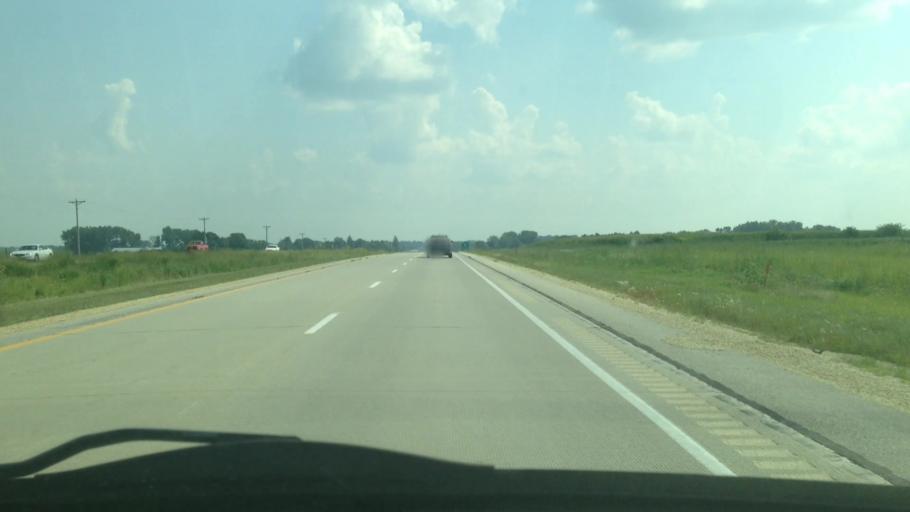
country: US
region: Iowa
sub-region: Bremer County
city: Denver
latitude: 42.7386
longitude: -92.3377
